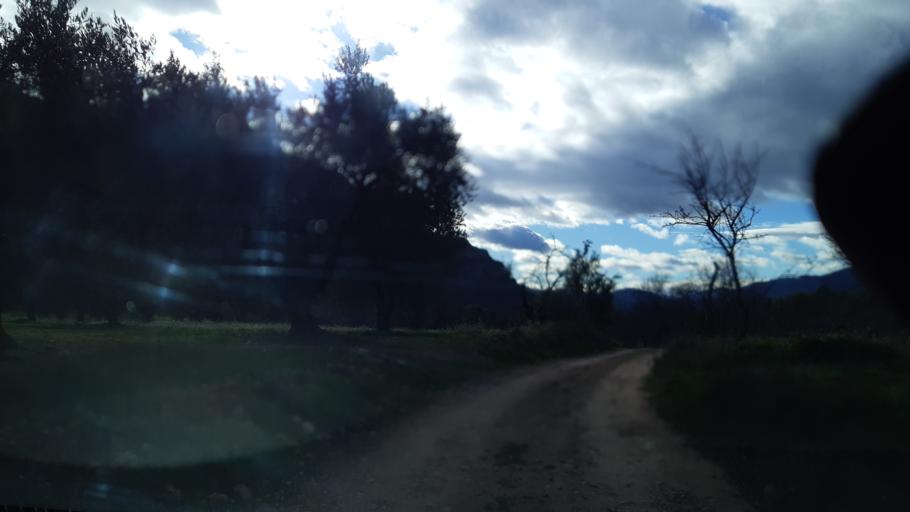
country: ES
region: Aragon
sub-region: Provincia de Teruel
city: Valderrobres
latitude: 40.8572
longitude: 0.2337
